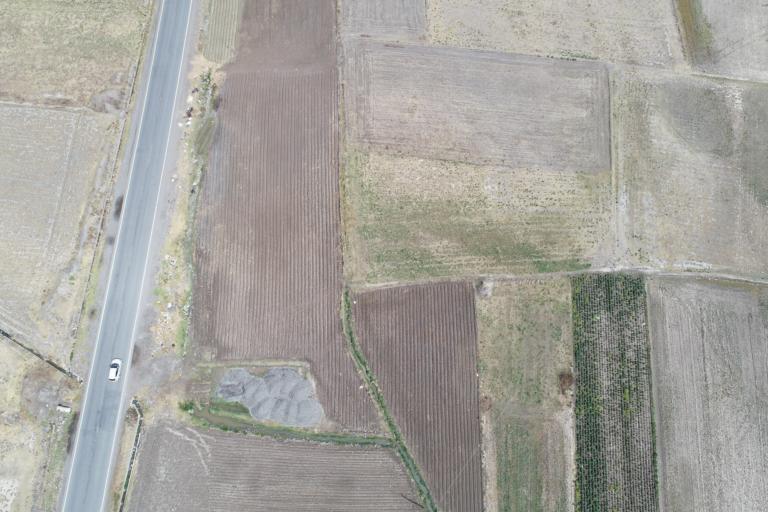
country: BO
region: La Paz
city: Achacachi
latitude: -16.0297
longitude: -68.6883
